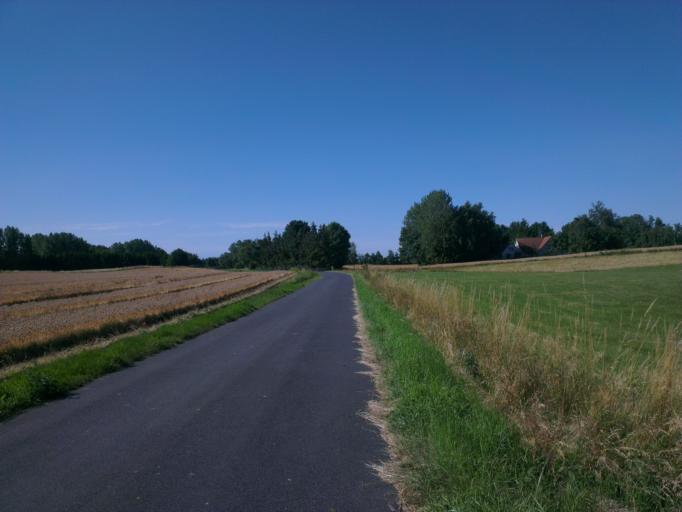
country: DK
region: Zealand
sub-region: Roskilde Kommune
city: Jyllinge
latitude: 55.7659
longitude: 12.0527
